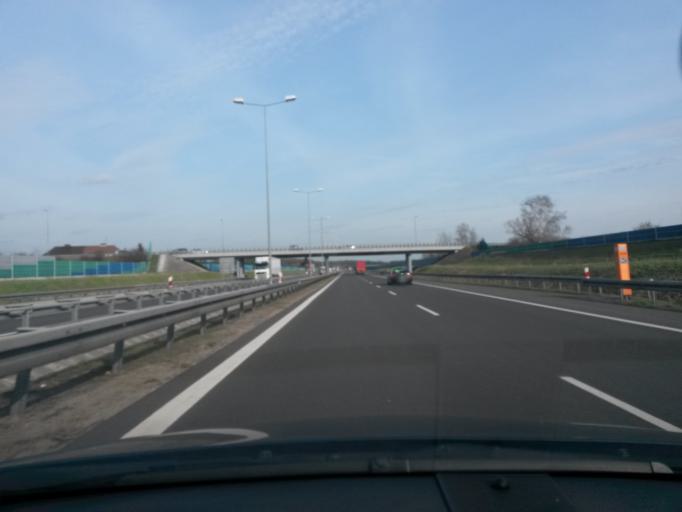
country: PL
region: Greater Poland Voivodeship
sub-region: Powiat wrzesinski
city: Wrzesnia
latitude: 52.3099
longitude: 17.5712
